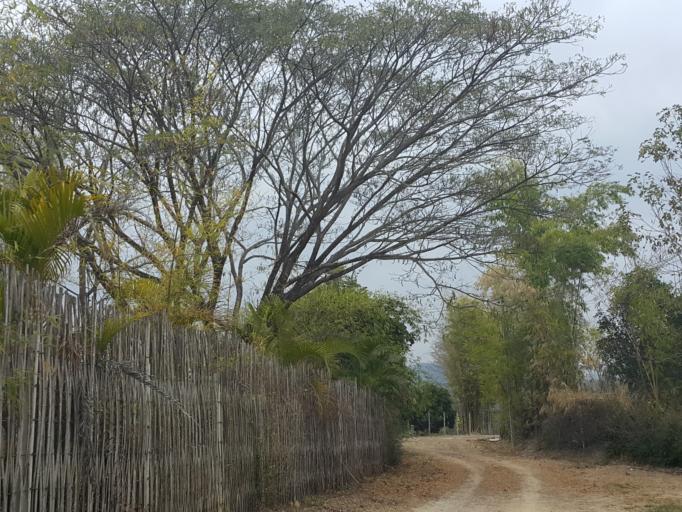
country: TH
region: Chiang Mai
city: Hang Dong
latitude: 18.7043
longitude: 98.8746
